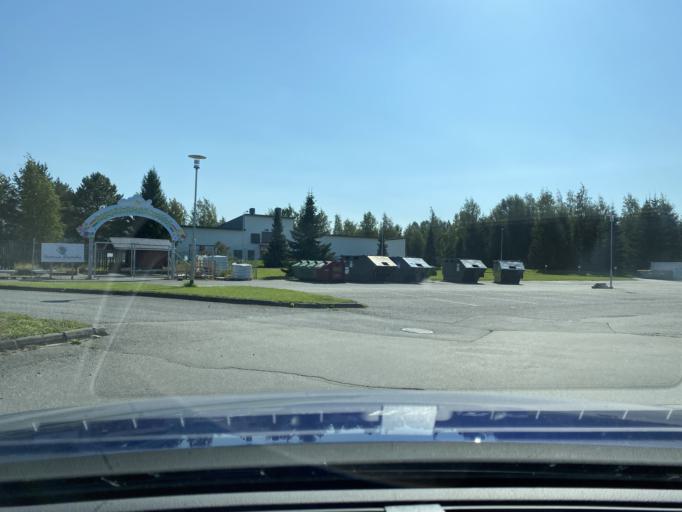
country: FI
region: Satakunta
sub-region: Rauma
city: Eura
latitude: 61.1292
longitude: 22.1372
